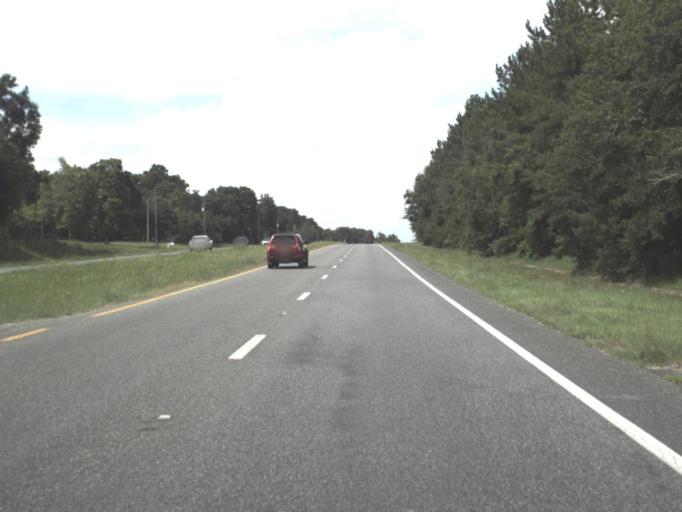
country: US
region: Florida
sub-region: Clay County
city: Middleburg
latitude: 30.0461
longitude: -81.8917
